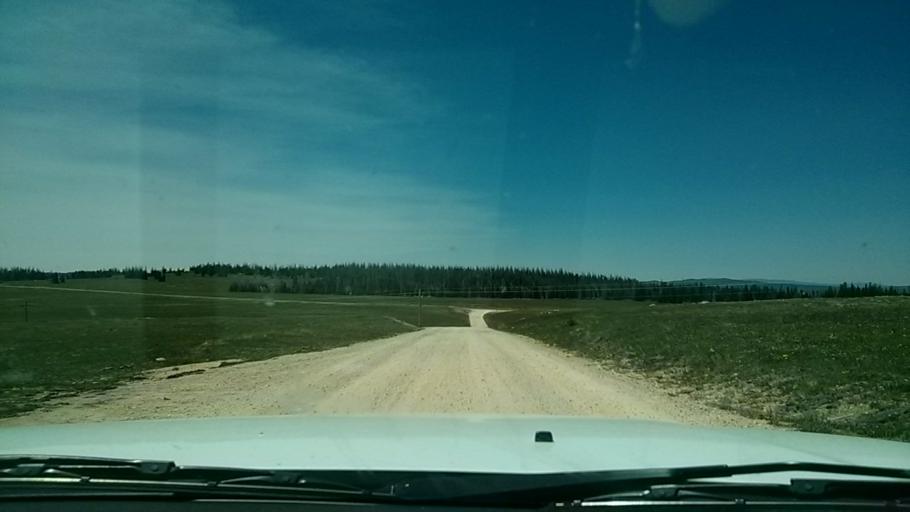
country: US
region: Utah
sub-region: Iron County
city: Parowan
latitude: 37.6723
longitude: -112.8355
